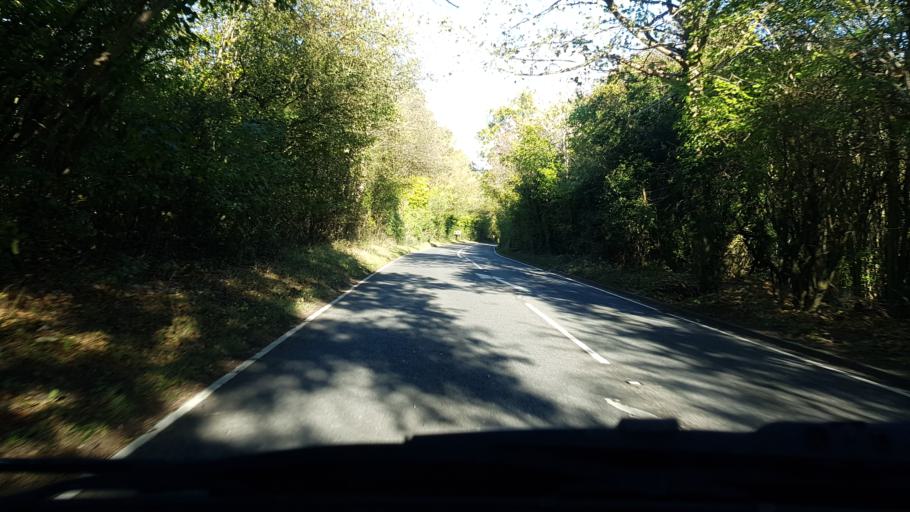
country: GB
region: England
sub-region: Surrey
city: Chilworth
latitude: 51.2413
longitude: -0.5049
